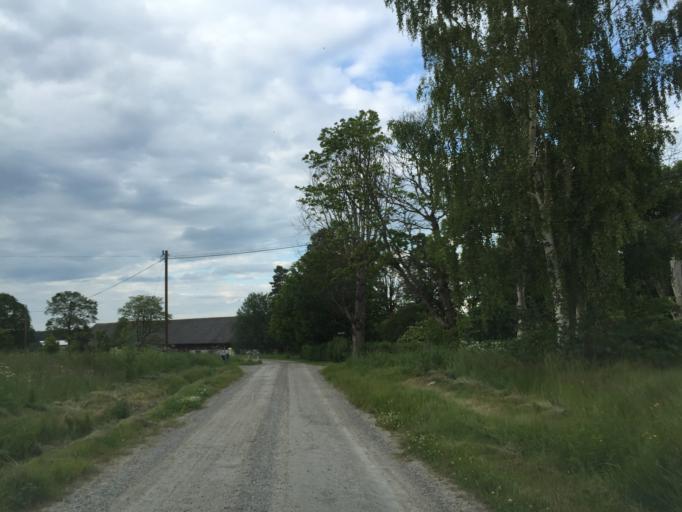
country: SE
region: OErebro
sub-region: Lindesbergs Kommun
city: Fellingsbro
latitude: 59.3274
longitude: 15.5314
